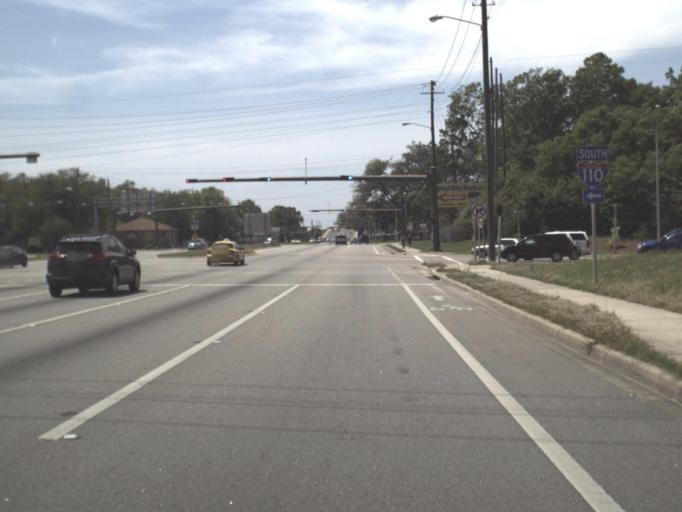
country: US
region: Florida
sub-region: Escambia County
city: Brent
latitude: 30.4723
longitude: -87.2286
